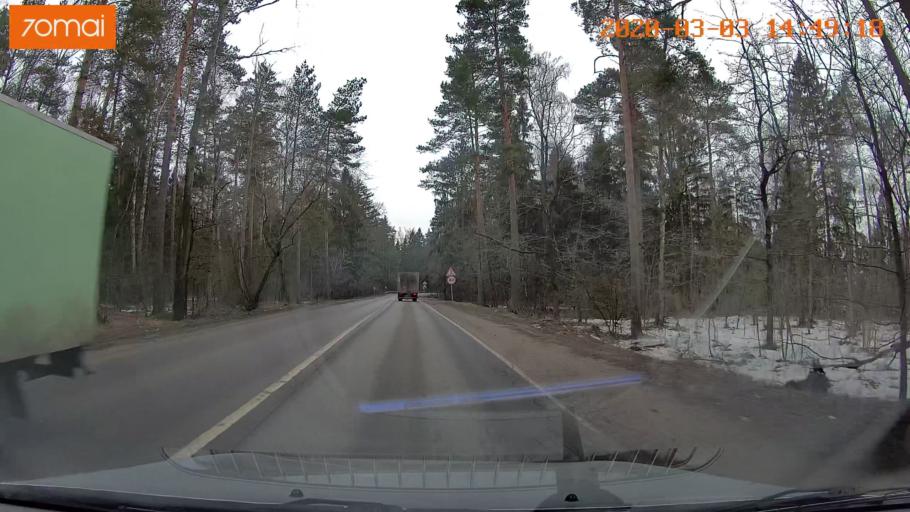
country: RU
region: Moskovskaya
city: Korenevo
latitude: 55.6774
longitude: 38.0398
